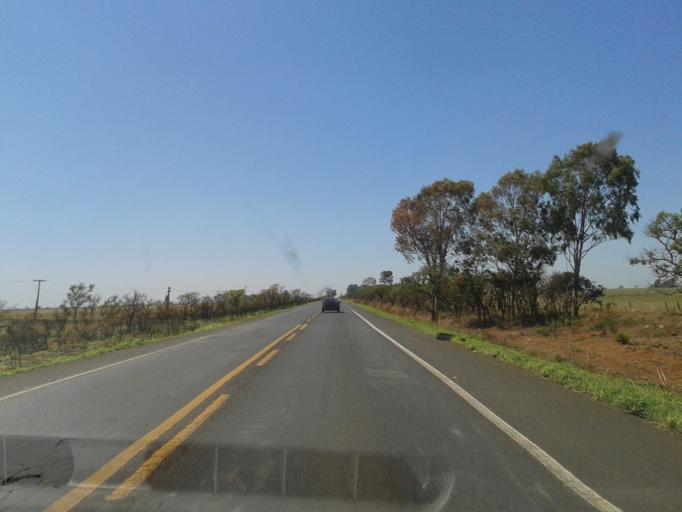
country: BR
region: Minas Gerais
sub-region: Uberaba
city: Uberaba
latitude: -19.3035
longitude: -47.5864
